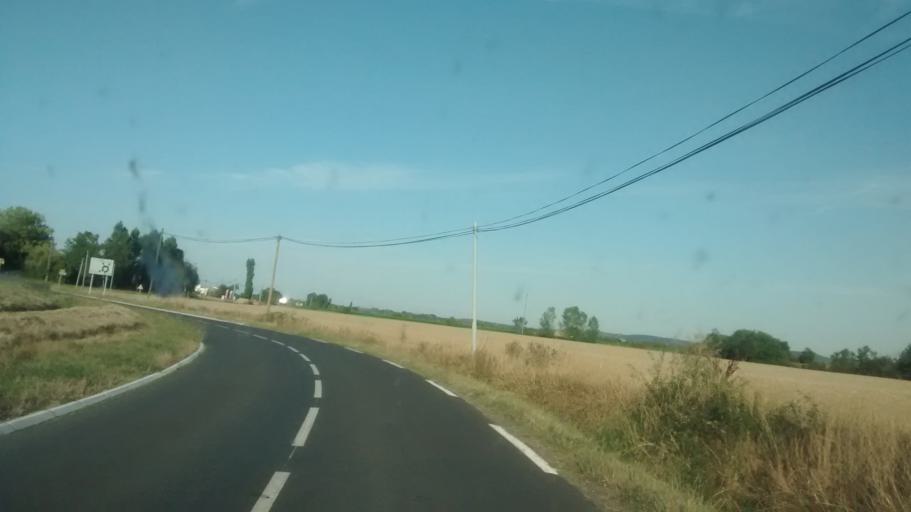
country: FR
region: Midi-Pyrenees
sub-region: Departement de la Haute-Garonne
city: Lherm
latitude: 43.4322
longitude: 1.2327
